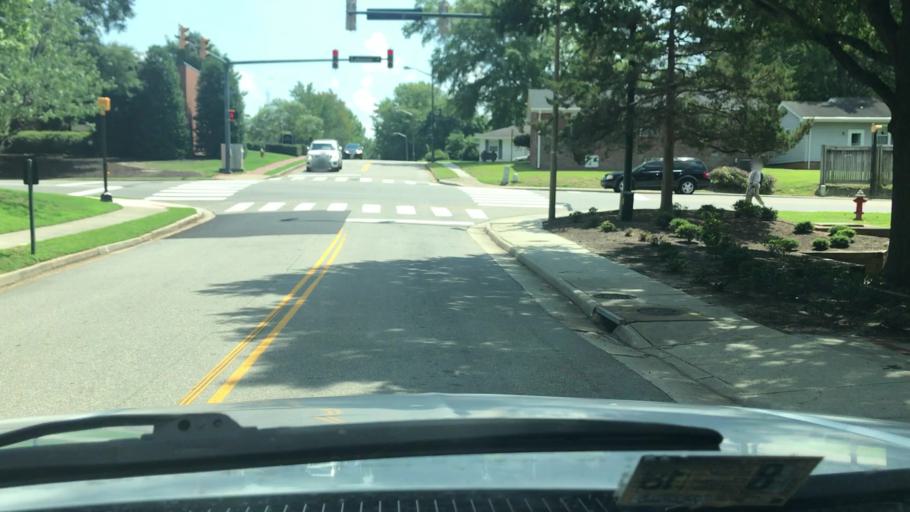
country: US
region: Virginia
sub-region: City of Williamsburg
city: Williamsburg
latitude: 37.2760
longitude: -76.7091
